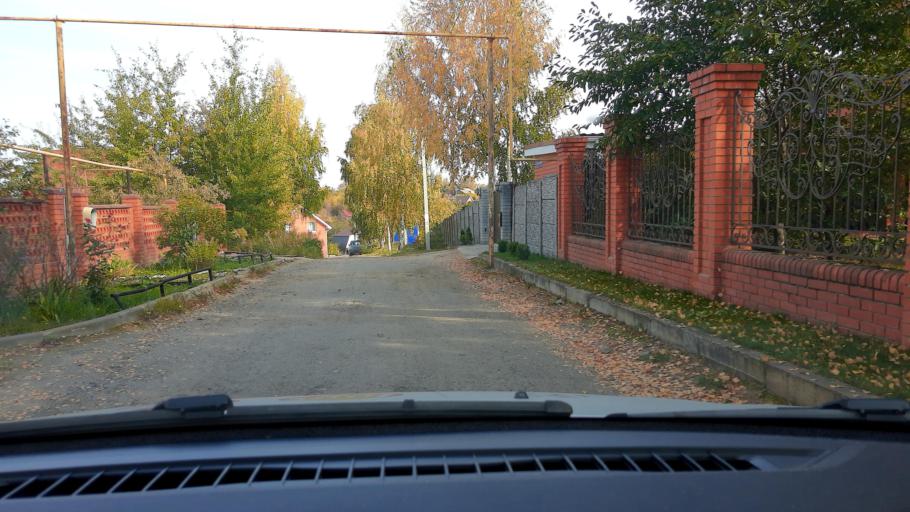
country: RU
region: Nizjnij Novgorod
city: Afonino
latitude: 56.2587
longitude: 44.0891
